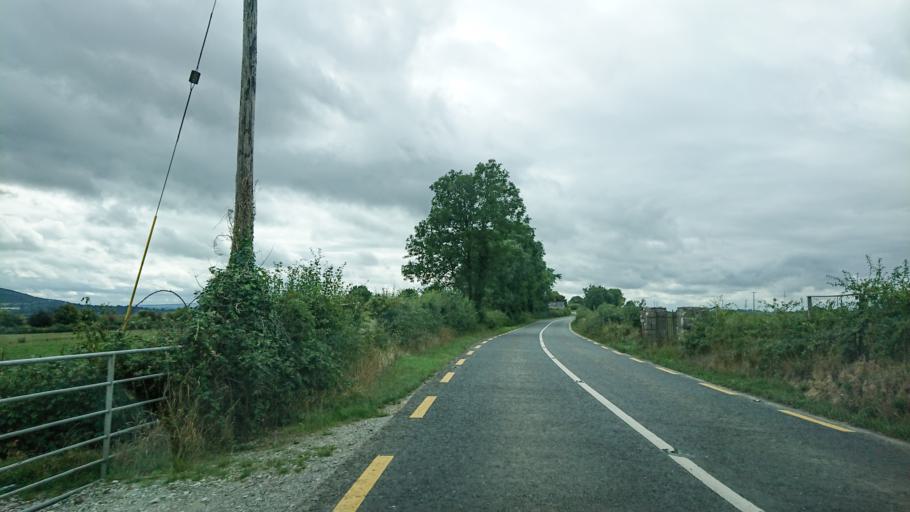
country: IE
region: Munster
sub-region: County Cork
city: Mallow
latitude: 52.1536
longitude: -8.5827
